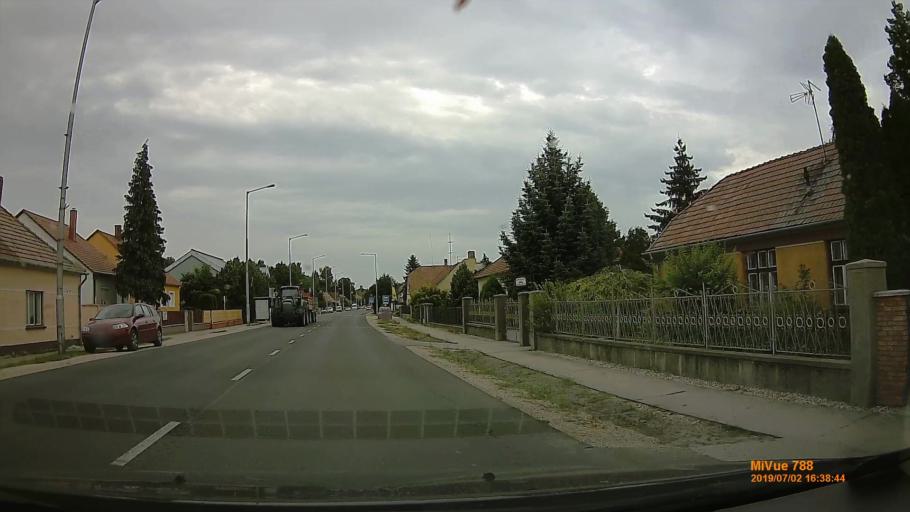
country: HU
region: Gyor-Moson-Sopron
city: Mosonmagyarovar
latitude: 47.8856
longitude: 17.2705
